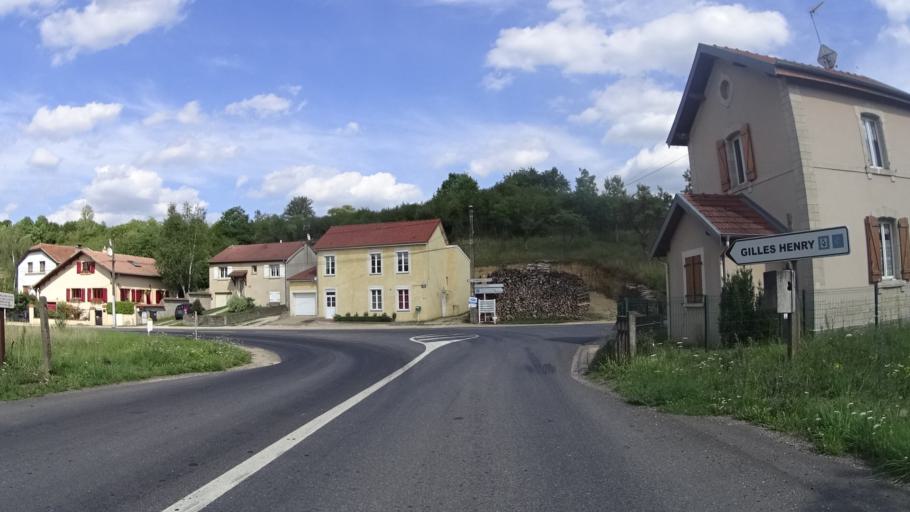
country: FR
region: Lorraine
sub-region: Departement de Meurthe-et-Moselle
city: Dommartin-les-Toul
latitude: 48.6589
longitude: 5.9019
